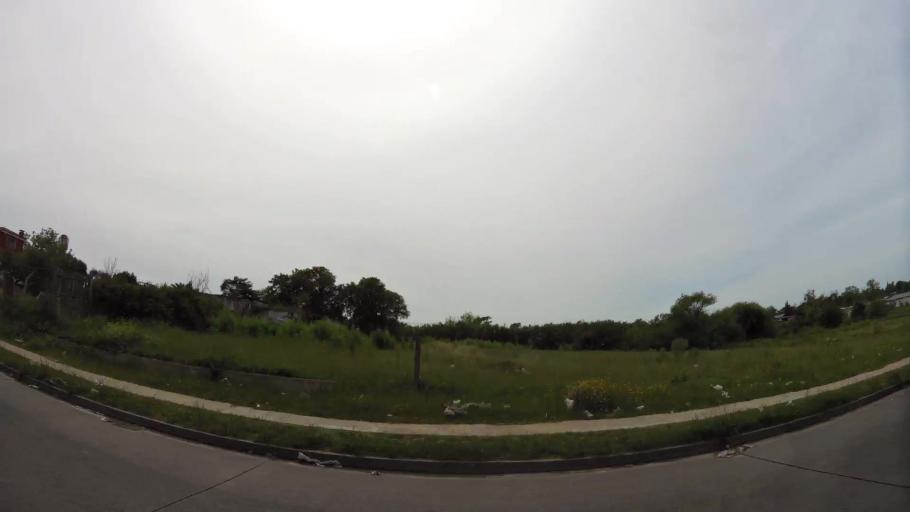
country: UY
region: Montevideo
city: Montevideo
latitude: -34.8363
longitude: -56.1683
